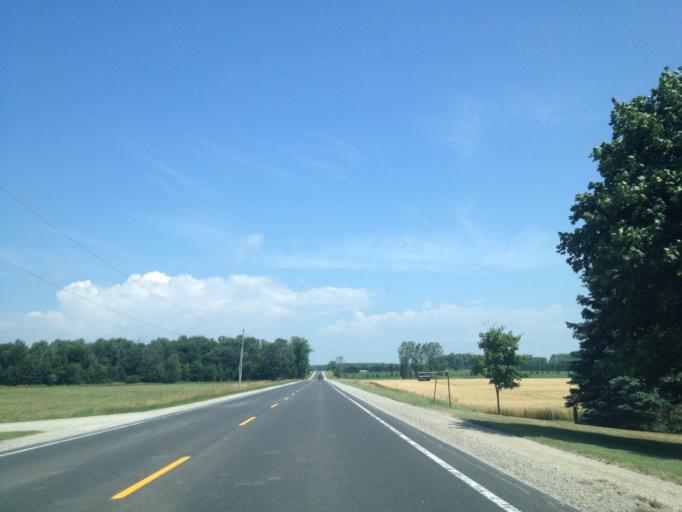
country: CA
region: Ontario
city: Huron East
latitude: 43.4216
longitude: -81.2229
